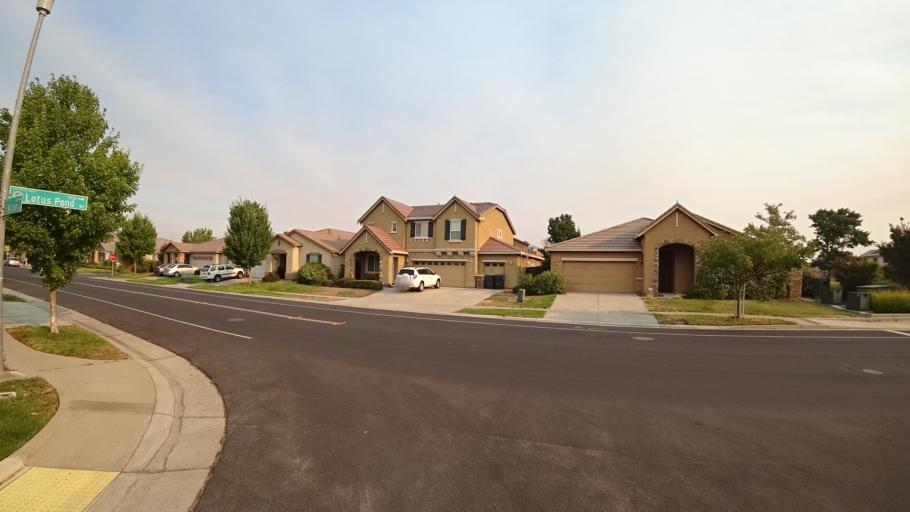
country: US
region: California
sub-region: Sacramento County
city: Laguna
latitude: 38.3890
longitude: -121.4410
